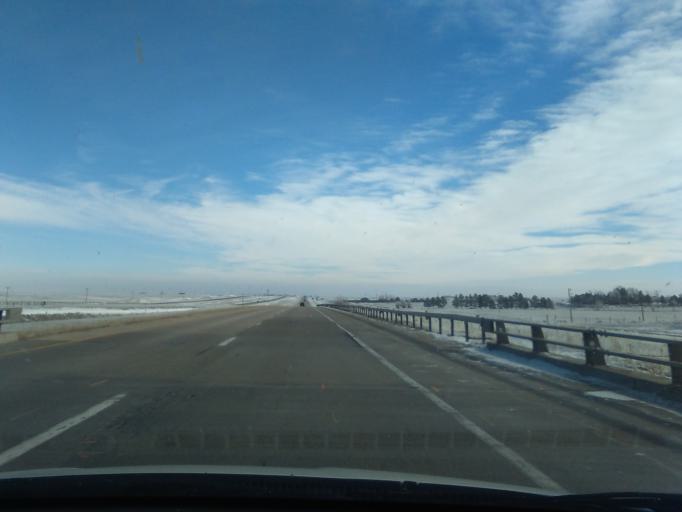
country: US
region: Wyoming
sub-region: Laramie County
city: Fox Farm-College
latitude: 41.1580
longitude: -104.5603
